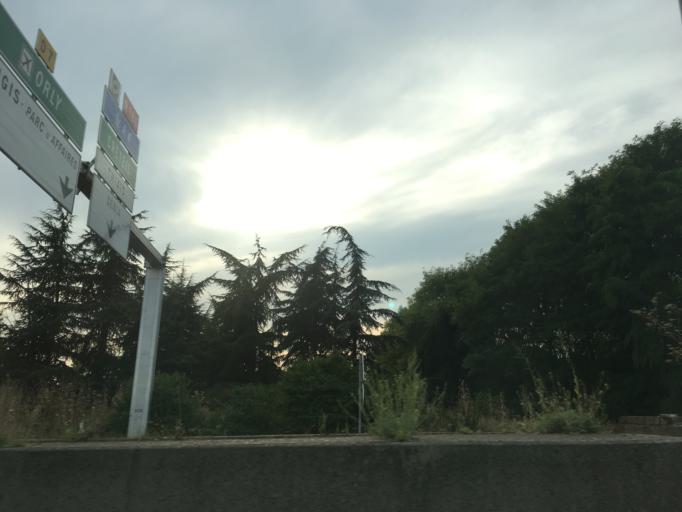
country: FR
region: Ile-de-France
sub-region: Departement du Val-de-Marne
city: Rungis
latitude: 48.7528
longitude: 2.3690
